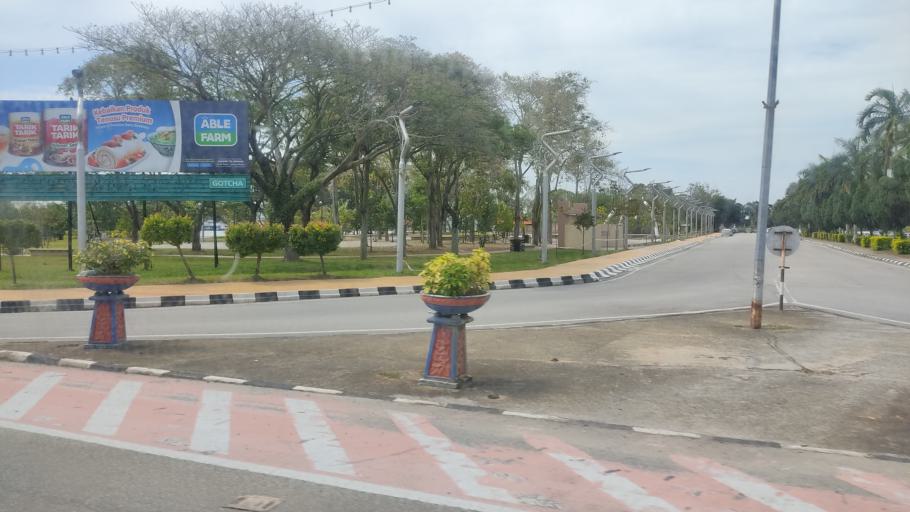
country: MY
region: Johor
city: Muar
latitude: 2.0527
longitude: 102.5655
